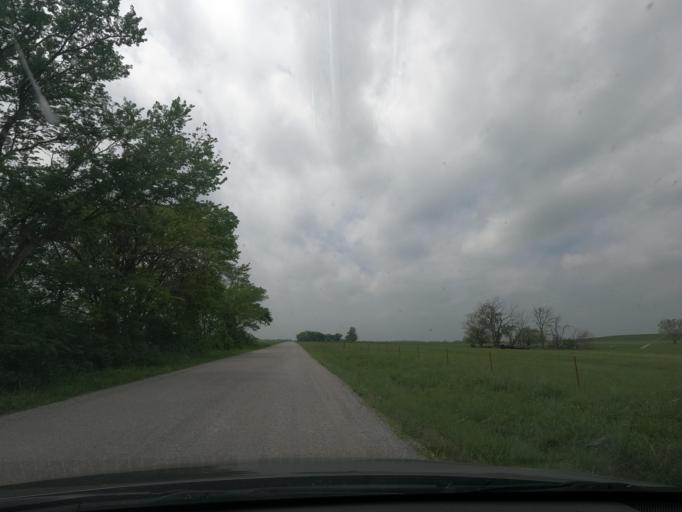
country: US
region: Kansas
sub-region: Cherokee County
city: Columbus
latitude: 37.2817
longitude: -94.9606
